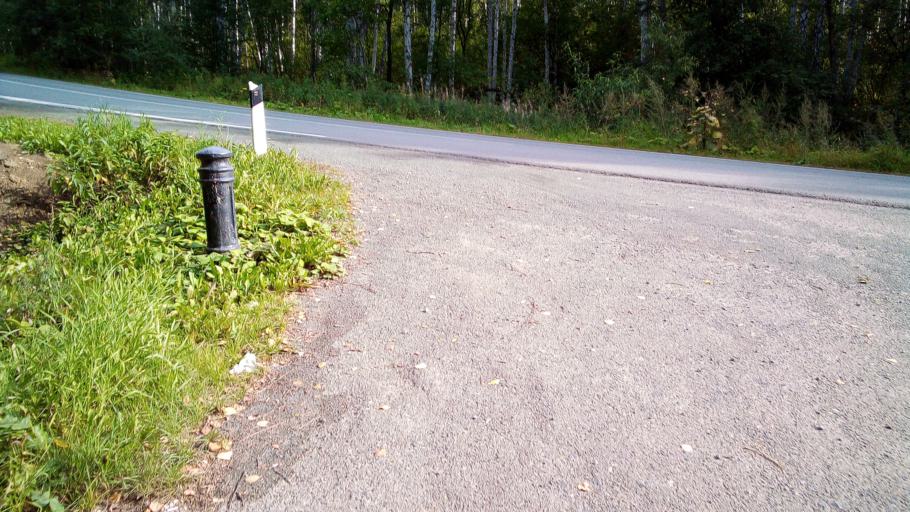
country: RU
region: Chelyabinsk
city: Tayginka
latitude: 55.4748
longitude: 60.4898
